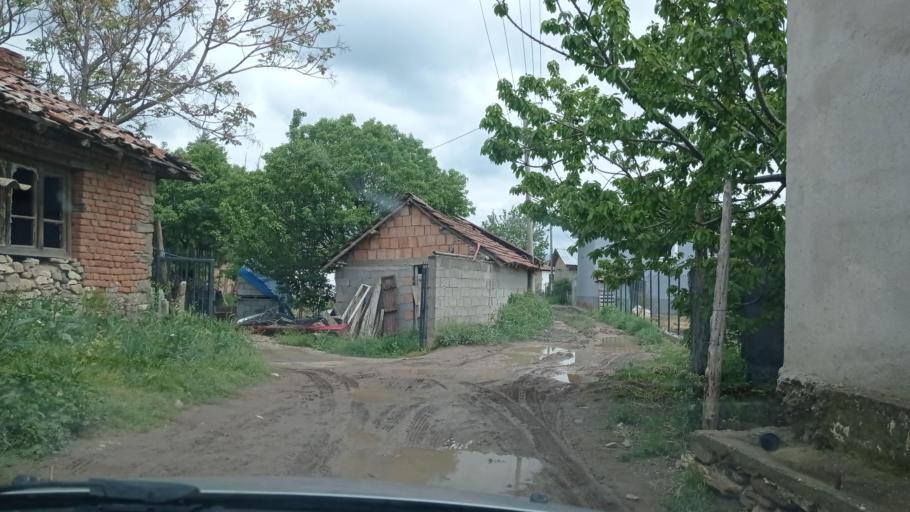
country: MK
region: Lozovo
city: Lozovo
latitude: 41.7642
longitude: 21.8931
